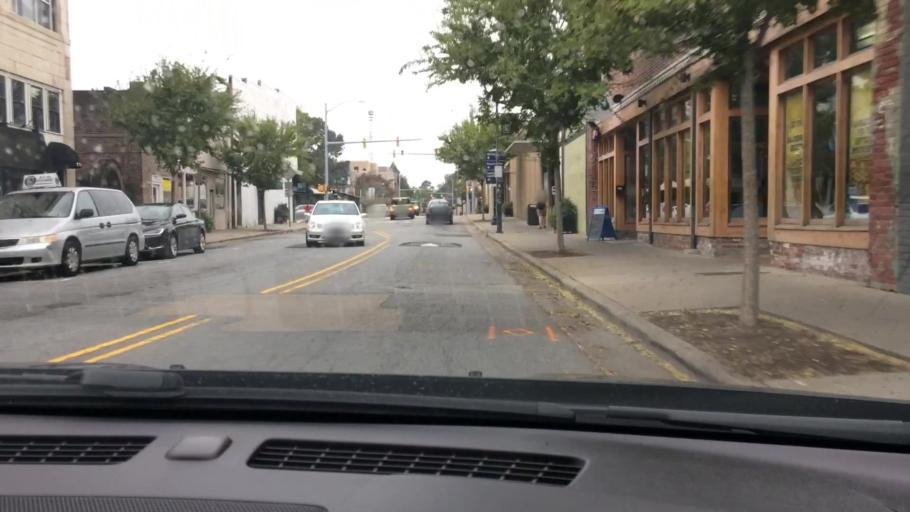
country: US
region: North Carolina
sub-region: Pitt County
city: Greenville
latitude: 35.6111
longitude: -77.3722
